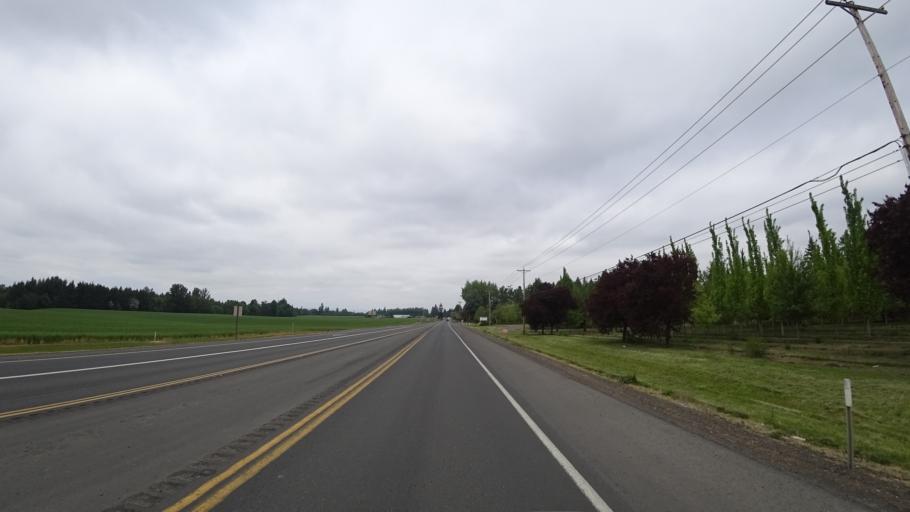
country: US
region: Oregon
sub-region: Washington County
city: Hillsboro
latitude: 45.4844
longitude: -122.9910
